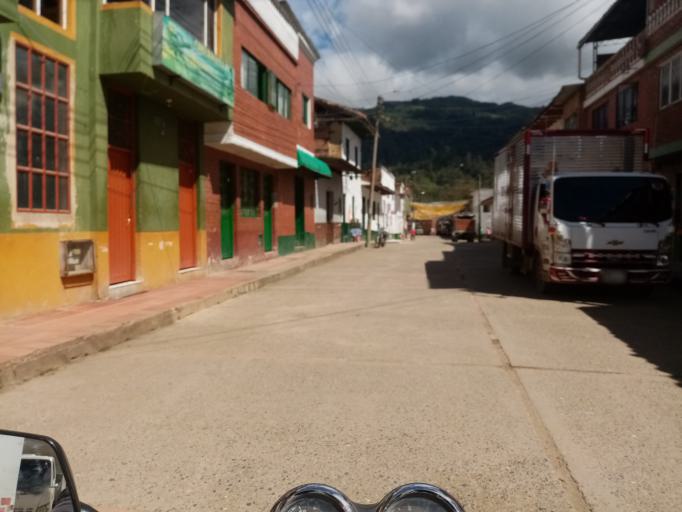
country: CO
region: Cundinamarca
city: Tenza
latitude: 5.0965
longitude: -73.4456
